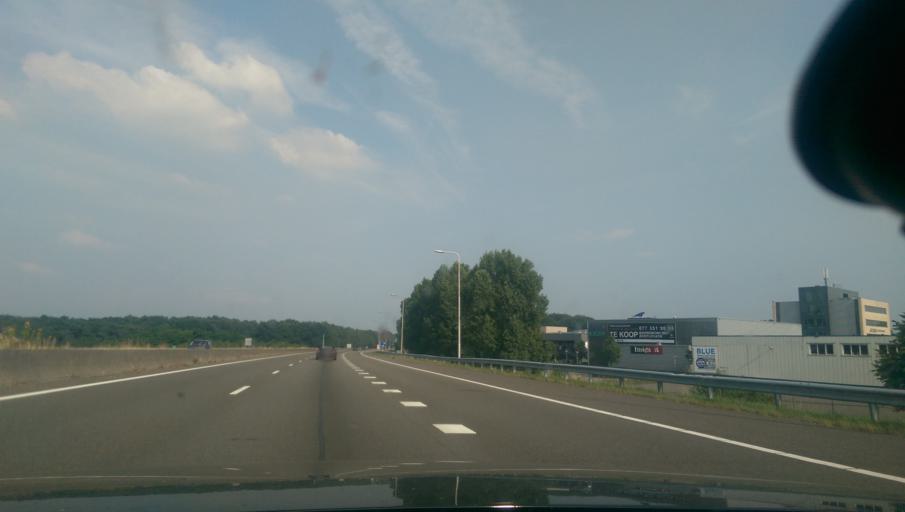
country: NL
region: Limburg
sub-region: Gemeente Venlo
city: Venlo
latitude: 51.3956
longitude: 6.1752
